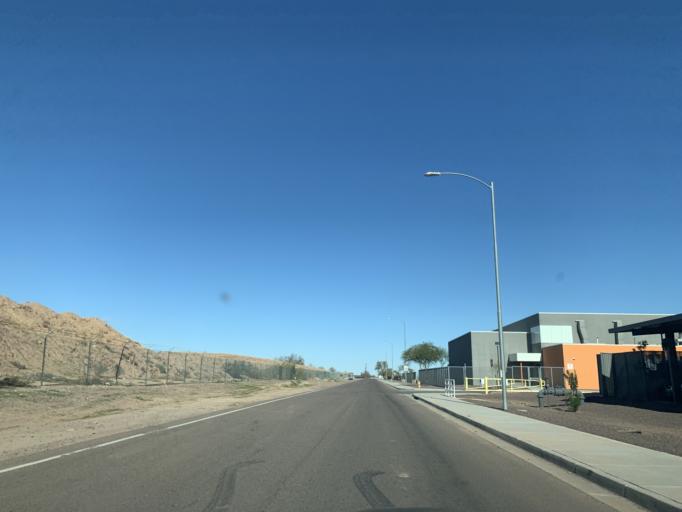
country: US
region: Arizona
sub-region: Maricopa County
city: Laveen
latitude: 33.3994
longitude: -112.1422
